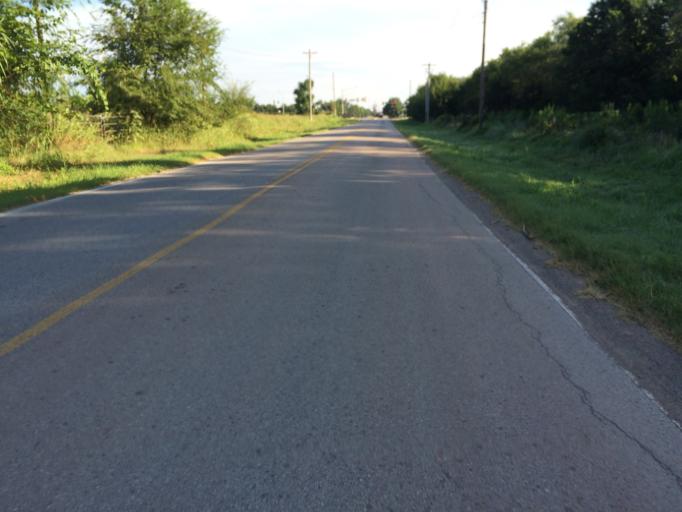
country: US
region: Oklahoma
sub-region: Cleveland County
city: Norman
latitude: 35.1786
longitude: -97.4413
